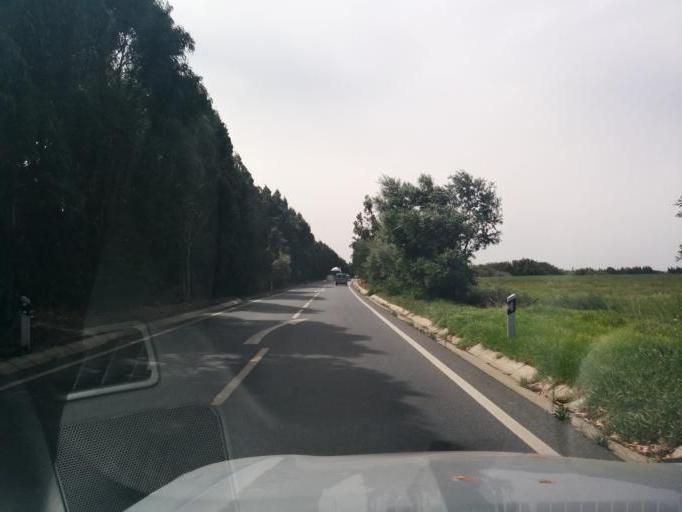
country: PT
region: Beja
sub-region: Odemira
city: Vila Nova de Milfontes
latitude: 37.6745
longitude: -8.7605
